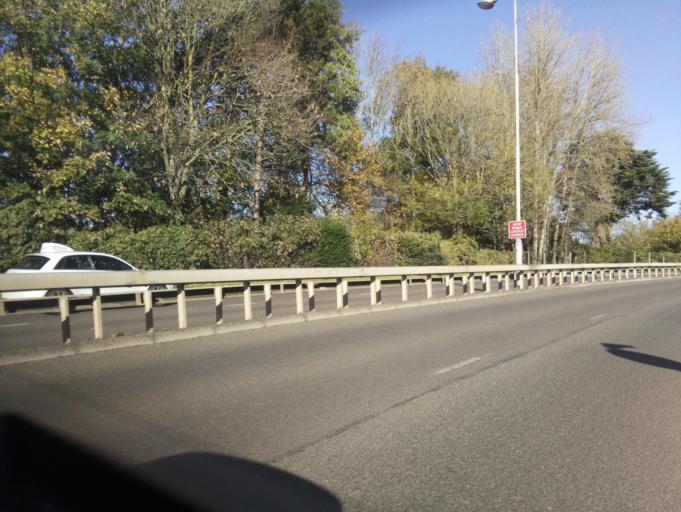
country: GB
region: England
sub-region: Somerset
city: Yeovil
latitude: 50.9427
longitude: -2.6383
